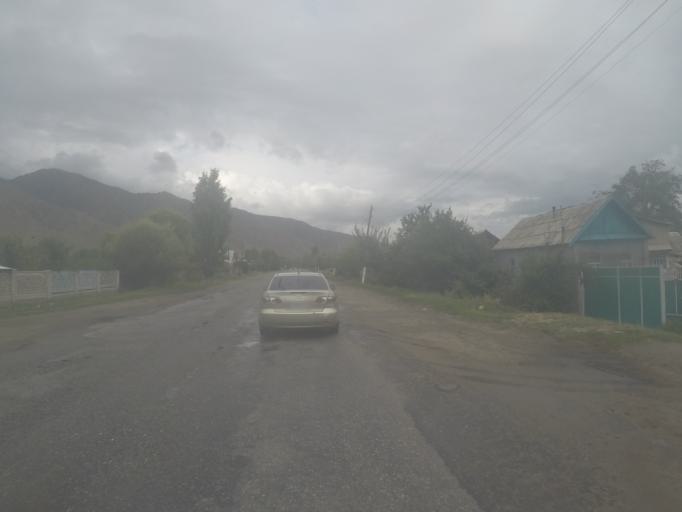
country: KG
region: Ysyk-Koel
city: Tyup
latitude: 42.7393
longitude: 78.0087
